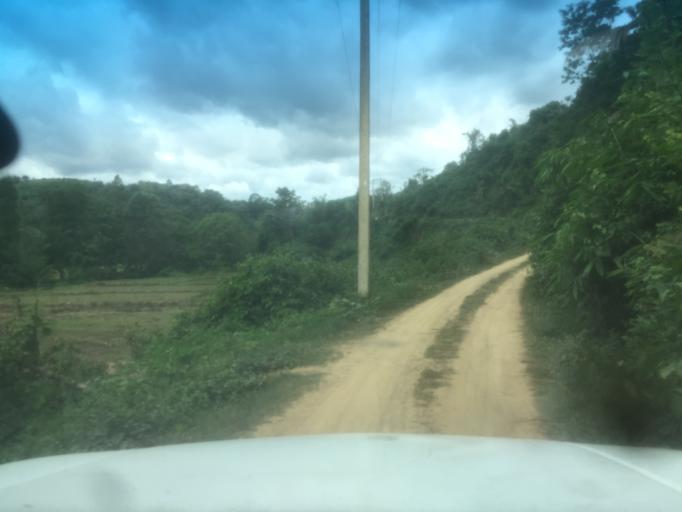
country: LA
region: Phongsali
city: Khoa
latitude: 20.9080
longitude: 102.5548
